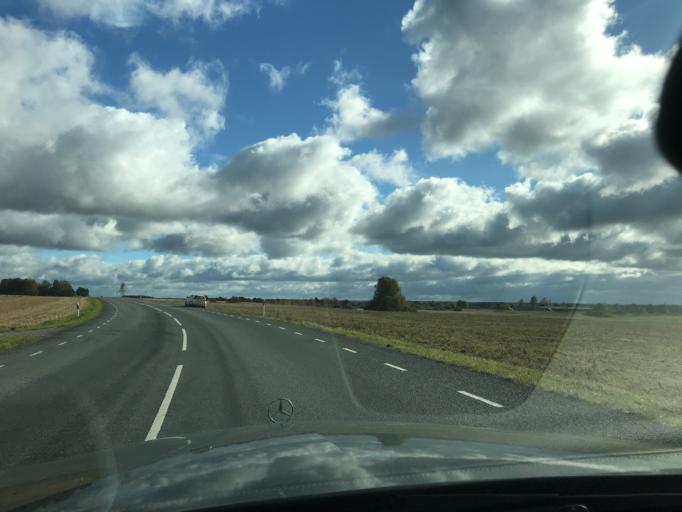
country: EE
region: Vorumaa
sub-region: Antsla vald
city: Vana-Antsla
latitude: 57.9163
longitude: 26.3553
